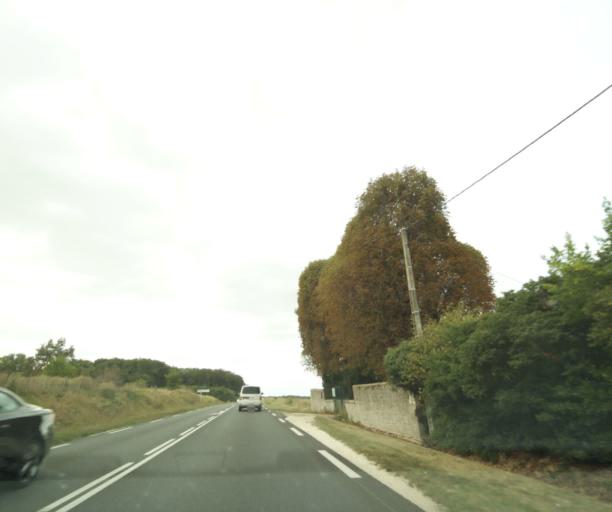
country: FR
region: Centre
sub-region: Departement d'Indre-et-Loire
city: Chambourg-sur-Indre
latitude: 47.1641
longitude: 0.9861
